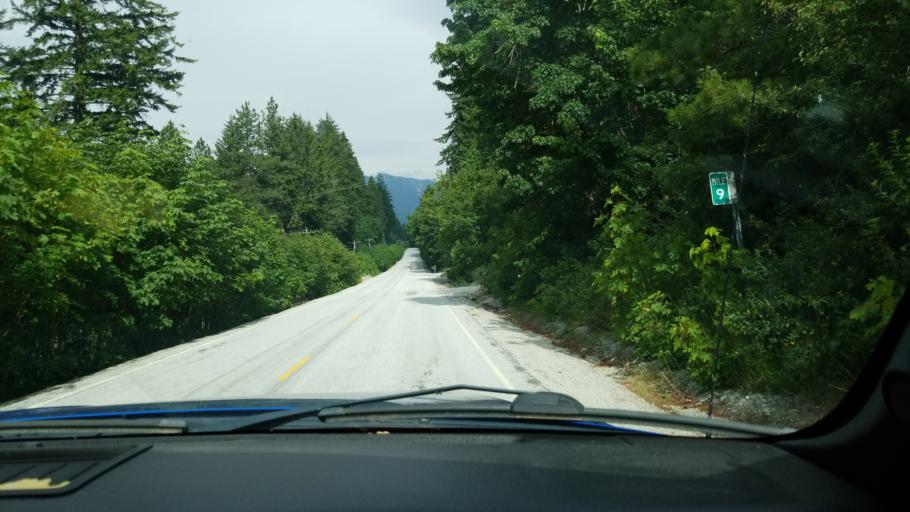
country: US
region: Washington
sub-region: Chelan County
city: Leavenworth
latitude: 47.8398
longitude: -120.8036
